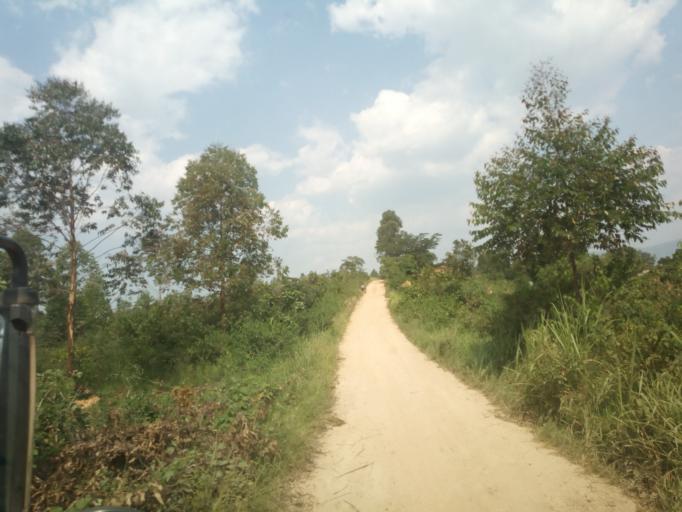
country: UG
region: Western Region
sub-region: Kanungu District
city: Ntungamo
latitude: -0.7926
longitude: 29.6611
